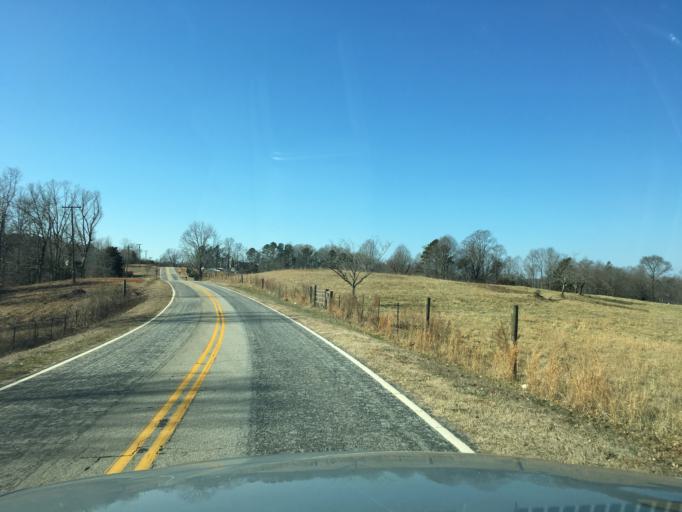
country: US
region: South Carolina
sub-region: Pickens County
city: Pickens
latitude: 34.8716
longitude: -82.7317
